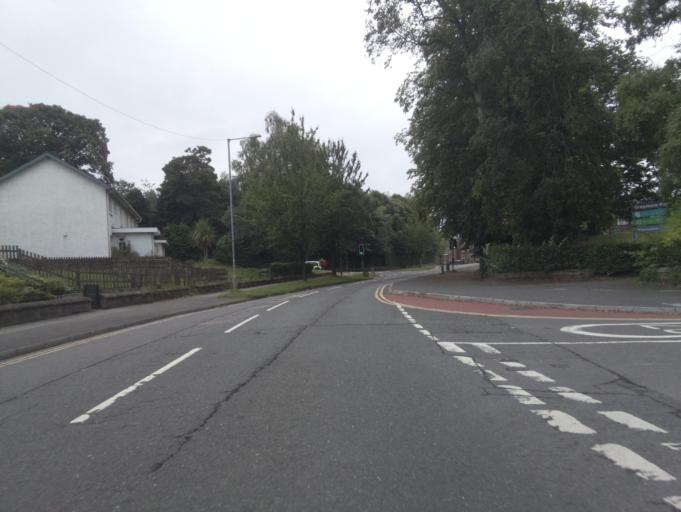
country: GB
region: Scotland
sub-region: Dumfries and Galloway
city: Dumfries
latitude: 55.0763
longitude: -3.5982
